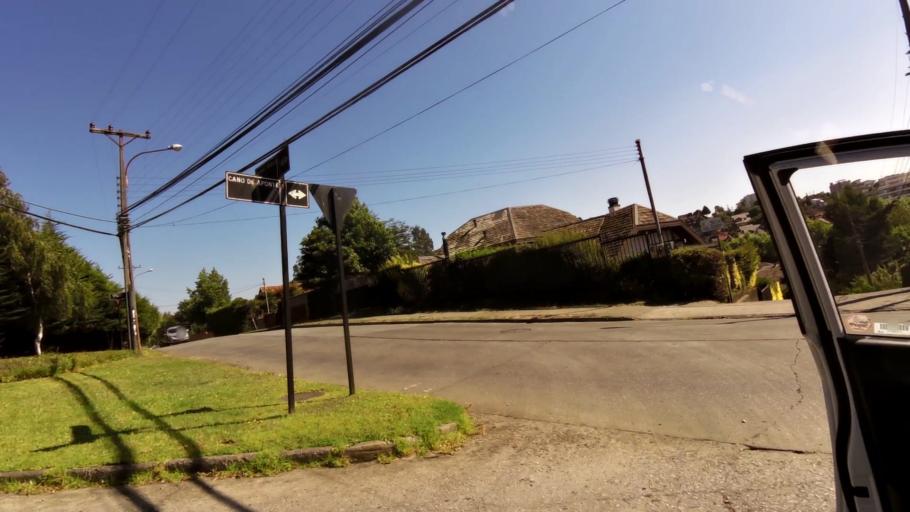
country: CL
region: Biobio
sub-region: Provincia de Concepcion
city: Concepcion
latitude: -36.7921
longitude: -73.0561
